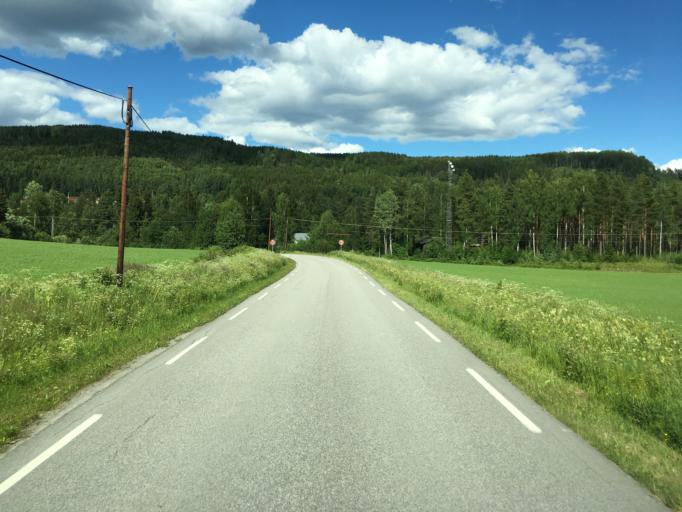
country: NO
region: Oppland
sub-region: Sondre Land
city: Hov
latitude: 60.5967
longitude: 10.2999
